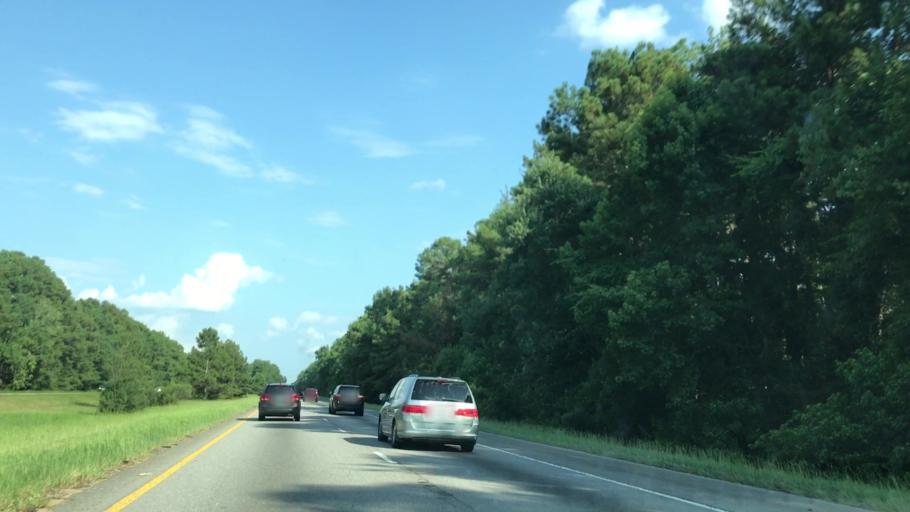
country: US
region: South Carolina
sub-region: Dorchester County
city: Saint George
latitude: 33.3836
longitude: -80.6280
